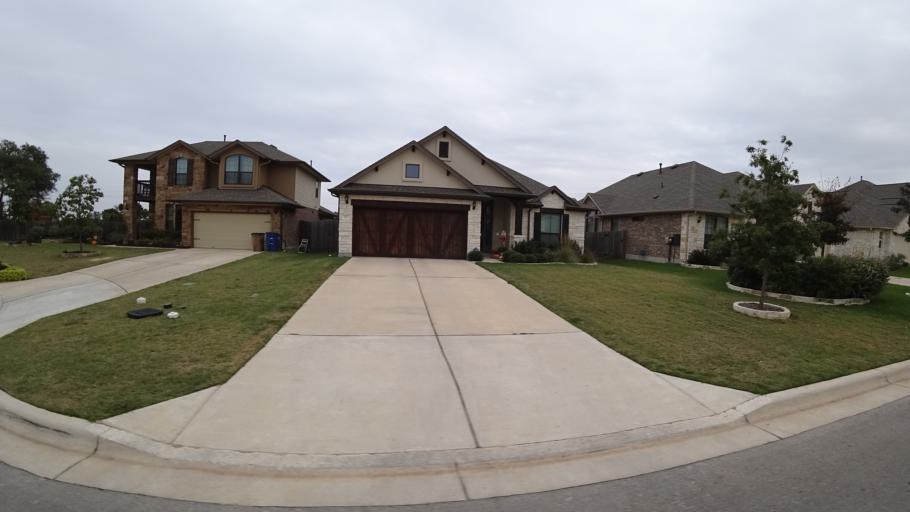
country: US
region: Texas
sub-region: Travis County
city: Shady Hollow
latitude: 30.1694
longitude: -97.8889
